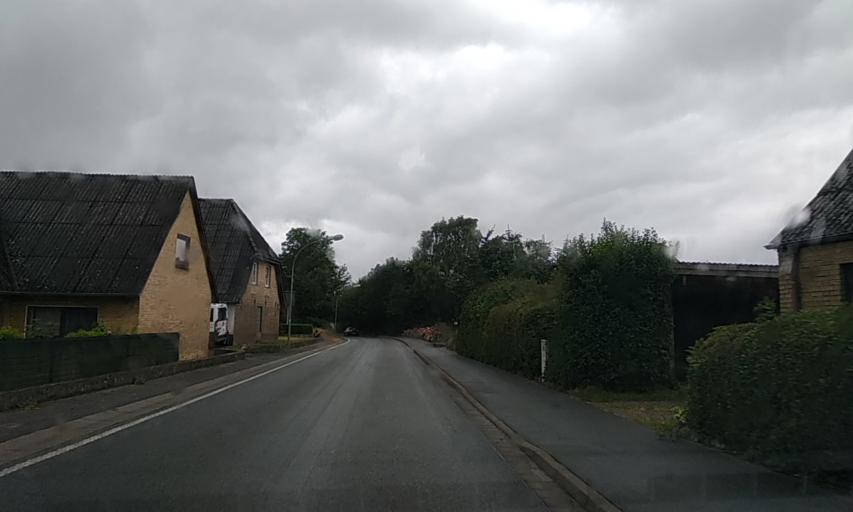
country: DE
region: Schleswig-Holstein
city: Neuberend
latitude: 54.5511
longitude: 9.5174
